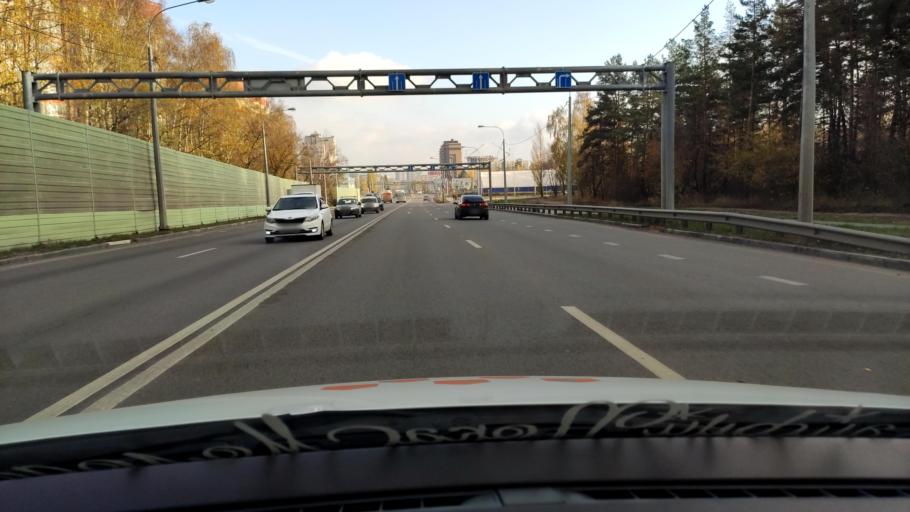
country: RU
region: Voronezj
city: Pridonskoy
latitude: 51.6851
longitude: 39.1134
